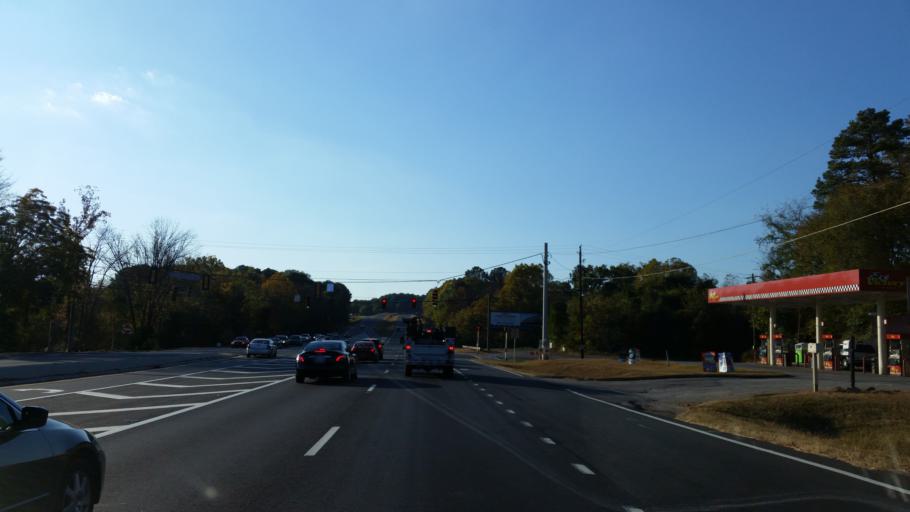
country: US
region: Georgia
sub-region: Bartow County
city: Cartersville
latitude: 34.2188
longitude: -84.8424
